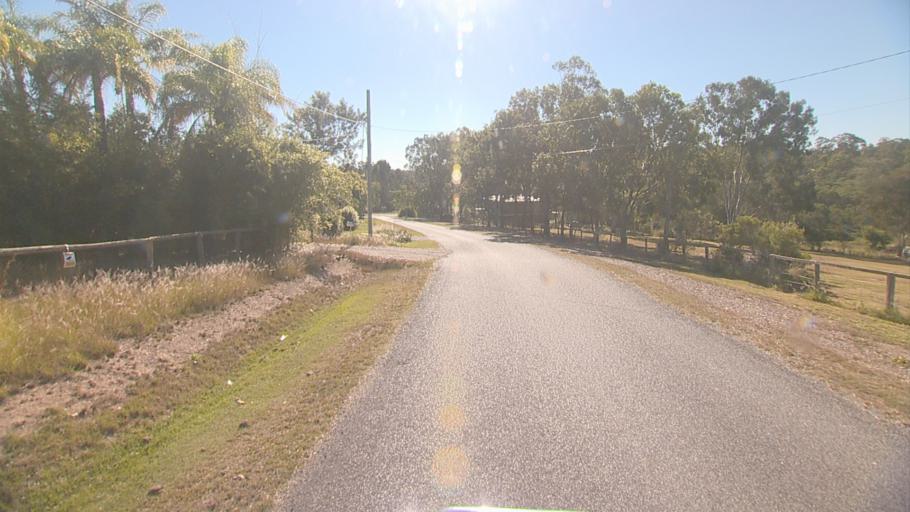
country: AU
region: Queensland
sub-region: Logan
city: Logan Reserve
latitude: -27.7434
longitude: 153.1232
